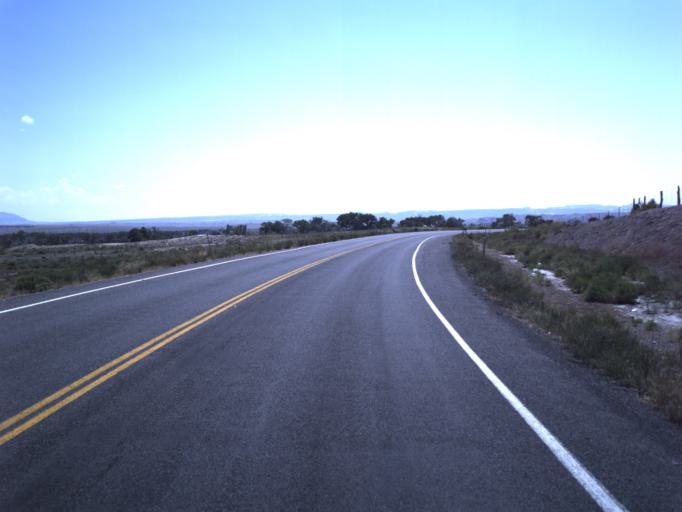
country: US
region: Utah
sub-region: Emery County
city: Orangeville
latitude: 39.2122
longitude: -111.0509
